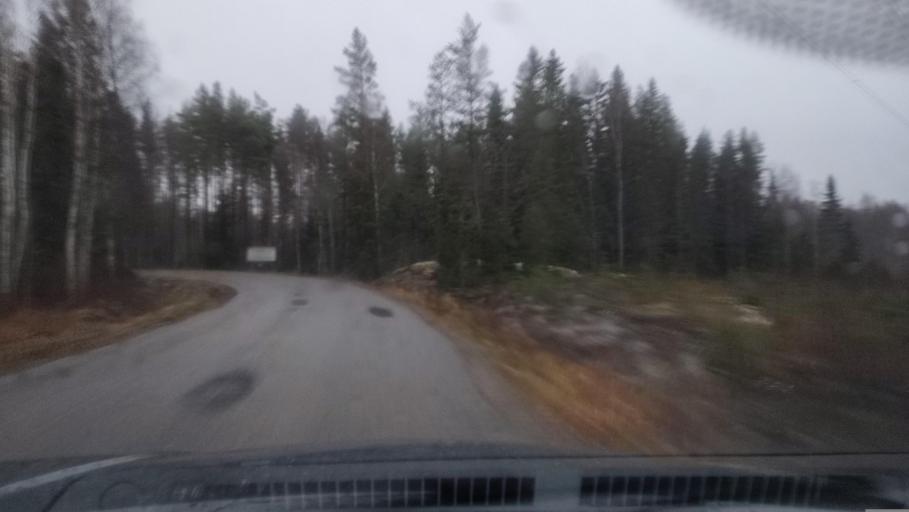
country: FI
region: Ostrobothnia
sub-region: Sydosterbotten
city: Kristinestad
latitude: 62.1486
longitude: 21.5532
